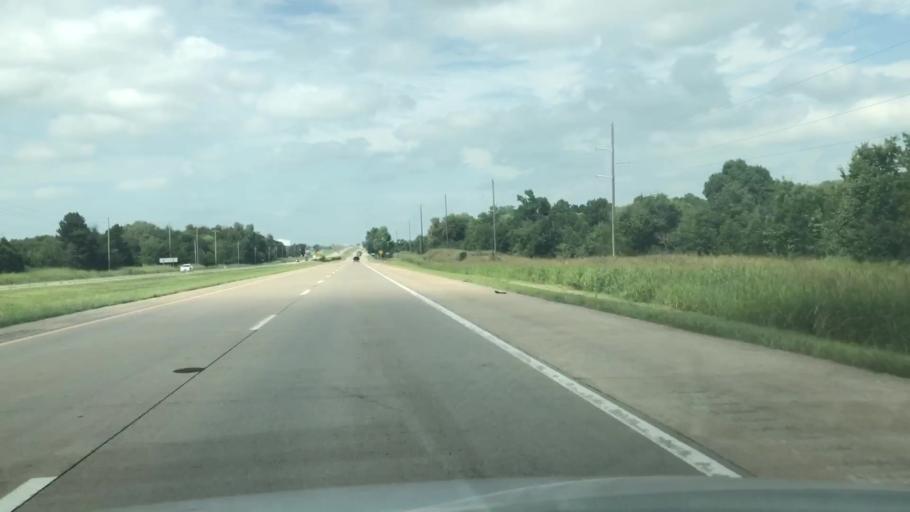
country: US
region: Oklahoma
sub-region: Osage County
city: Skiatook
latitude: 36.5518
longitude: -95.9286
